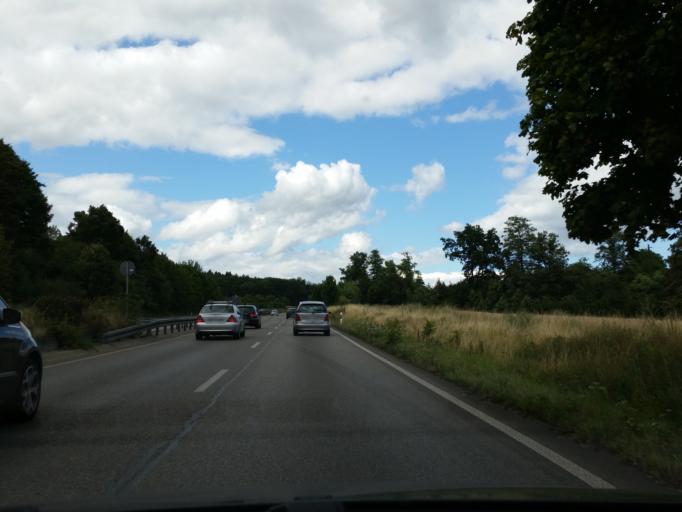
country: DE
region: Baden-Wuerttemberg
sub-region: Regierungsbezirk Stuttgart
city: Nurtingen
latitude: 48.6434
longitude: 9.3320
